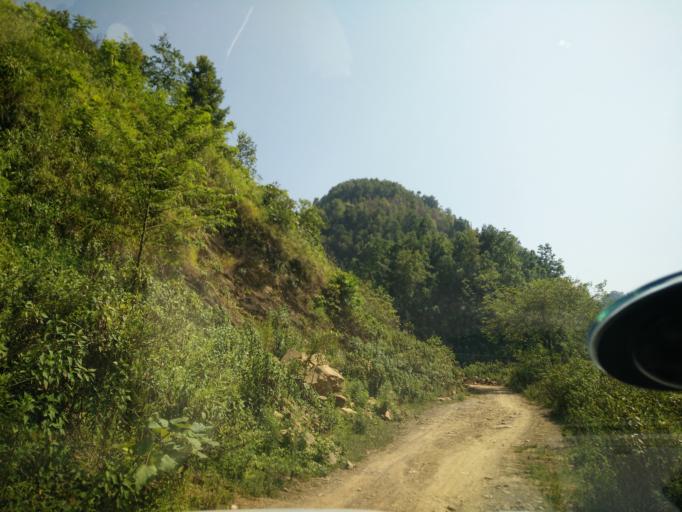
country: CN
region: Guangxi Zhuangzu Zizhiqu
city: Xinzhou
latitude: 25.1832
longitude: 105.6881
